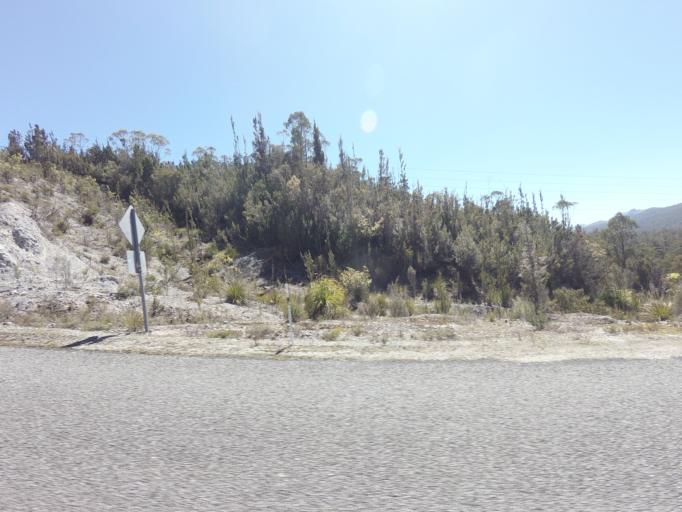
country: AU
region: Tasmania
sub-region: Huon Valley
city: Geeveston
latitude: -42.8137
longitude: 146.3719
